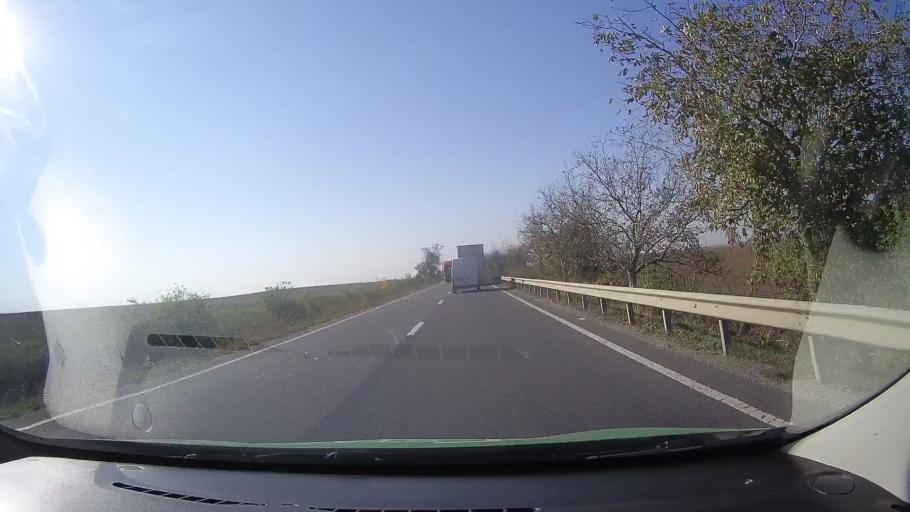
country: RO
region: Satu Mare
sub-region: Comuna Petresti
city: Petresti
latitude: 47.6378
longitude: 22.4018
